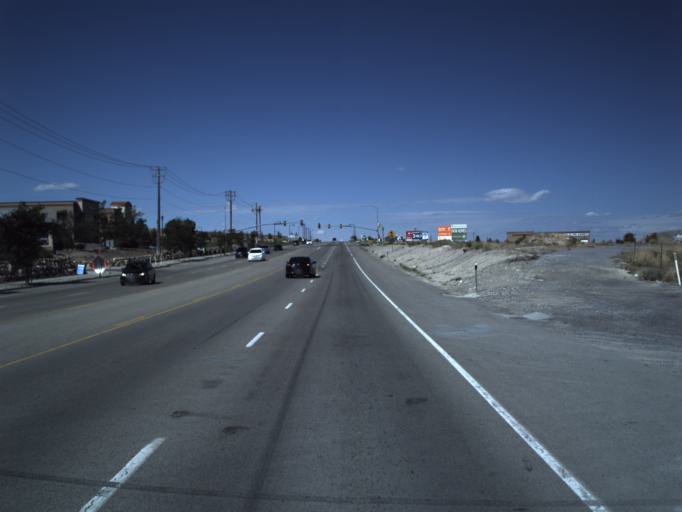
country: US
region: Utah
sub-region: Utah County
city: Saratoga Springs
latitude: 40.3971
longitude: -111.9185
